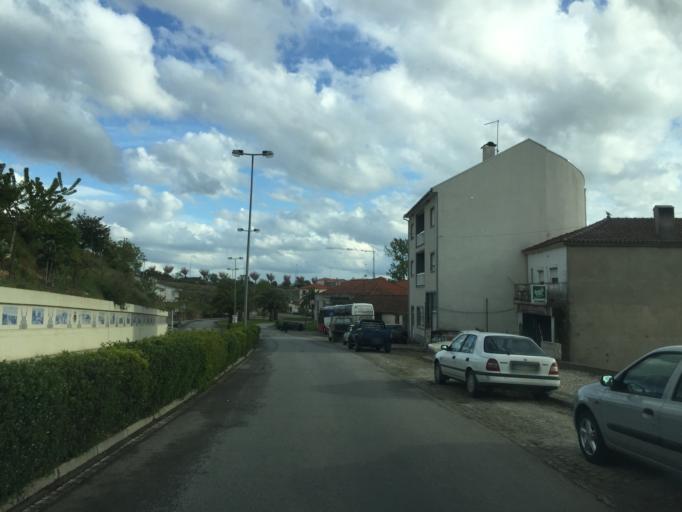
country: PT
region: Braganca
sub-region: Alfandega da Fe
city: Alfandega da Fe
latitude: 41.3390
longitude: -6.9628
